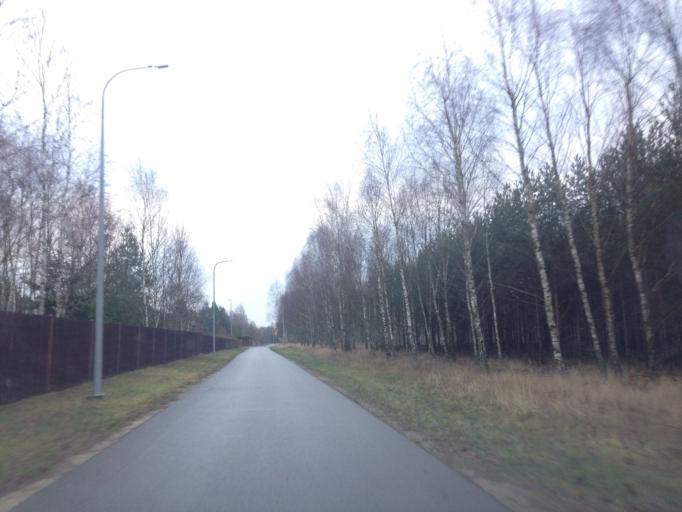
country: PL
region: Kujawsko-Pomorskie
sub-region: Powiat torunski
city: Wielka Nieszawka
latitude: 52.9891
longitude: 18.4433
